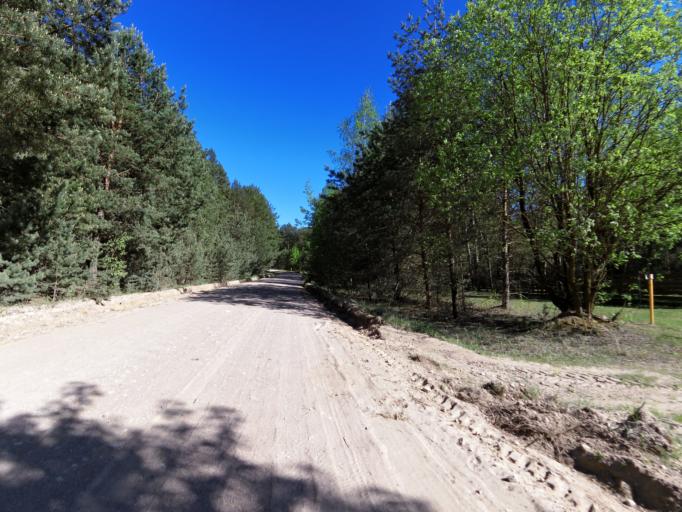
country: LT
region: Vilnius County
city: Pilaite
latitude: 54.6772
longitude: 25.1652
